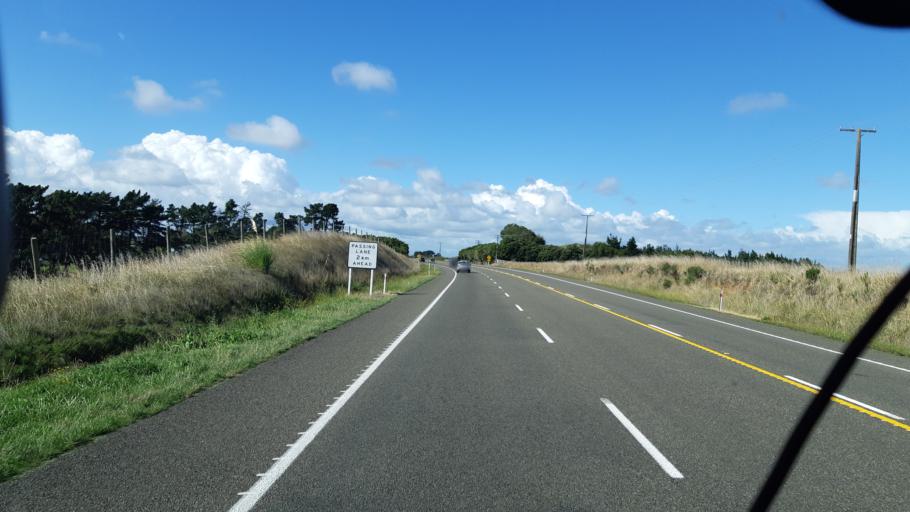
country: NZ
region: Manawatu-Wanganui
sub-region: Wanganui District
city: Wanganui
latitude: -39.9740
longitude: 175.1167
